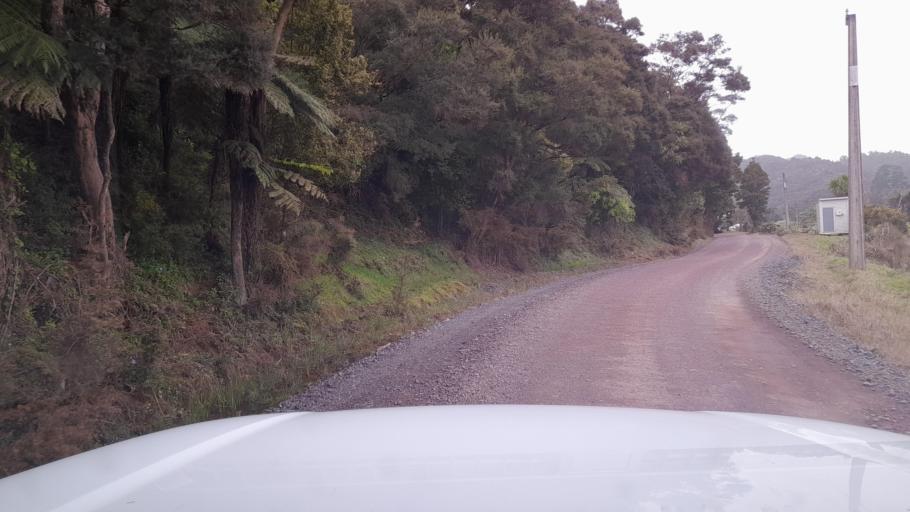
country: NZ
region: Northland
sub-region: Far North District
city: Paihia
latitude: -35.3359
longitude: 174.2308
